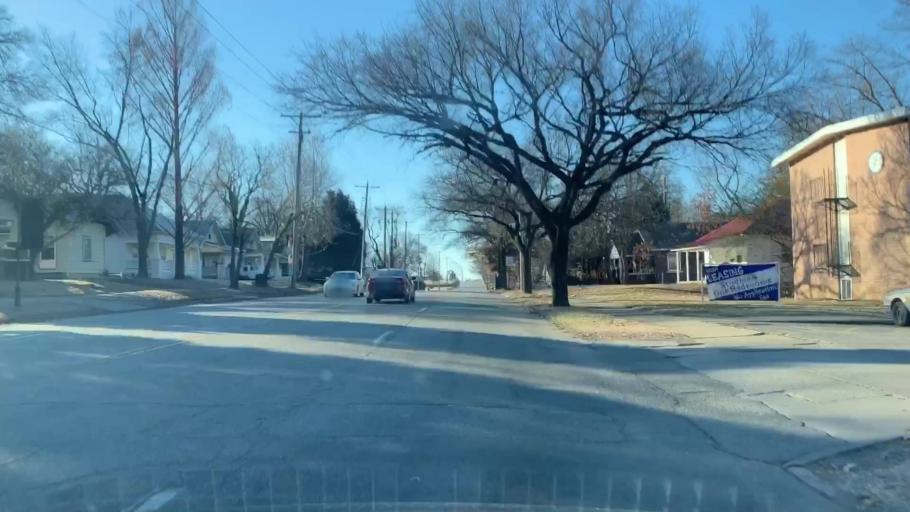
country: US
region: Kansas
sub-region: Crawford County
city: Pittsburg
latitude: 37.3888
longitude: -94.7052
